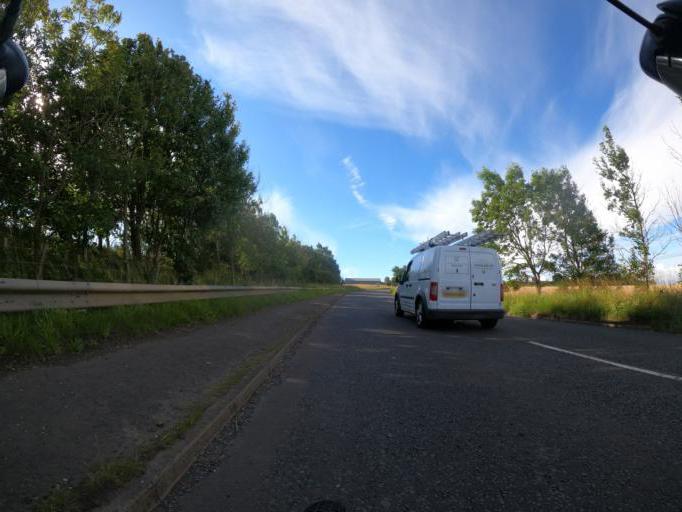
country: GB
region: Scotland
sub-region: Edinburgh
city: Newbridge
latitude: 55.9126
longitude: -3.4064
